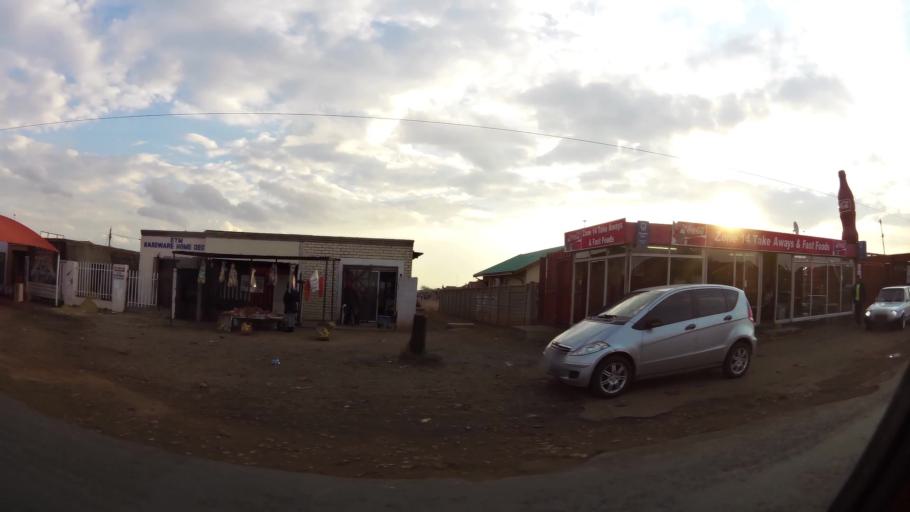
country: ZA
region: Gauteng
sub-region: City of Johannesburg Metropolitan Municipality
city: Orange Farm
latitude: -26.5899
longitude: 27.8469
